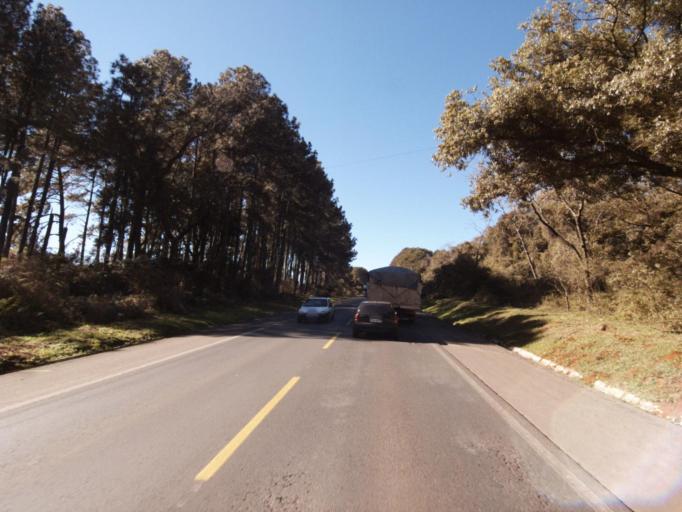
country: BR
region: Santa Catarina
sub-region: Xanxere
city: Xanxere
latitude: -26.9117
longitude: -52.4735
